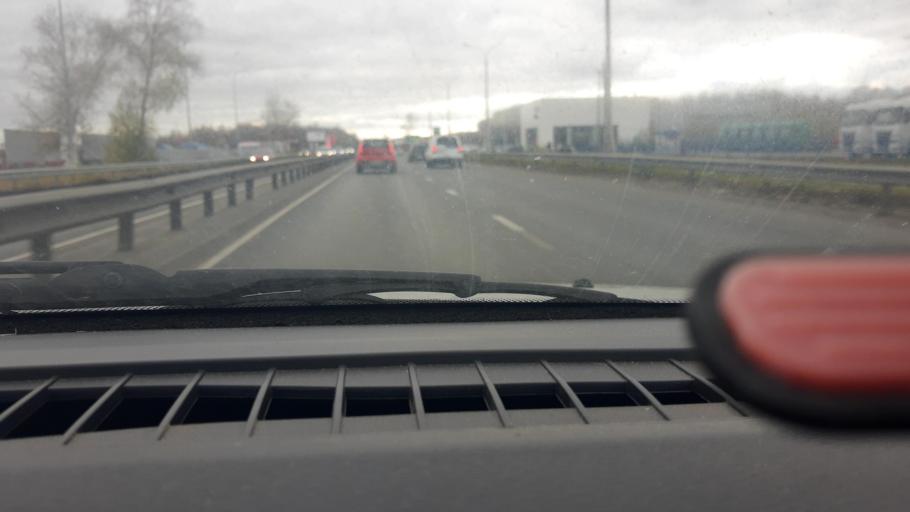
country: RU
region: Nizjnij Novgorod
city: Gorbatovka
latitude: 56.3103
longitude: 43.7950
